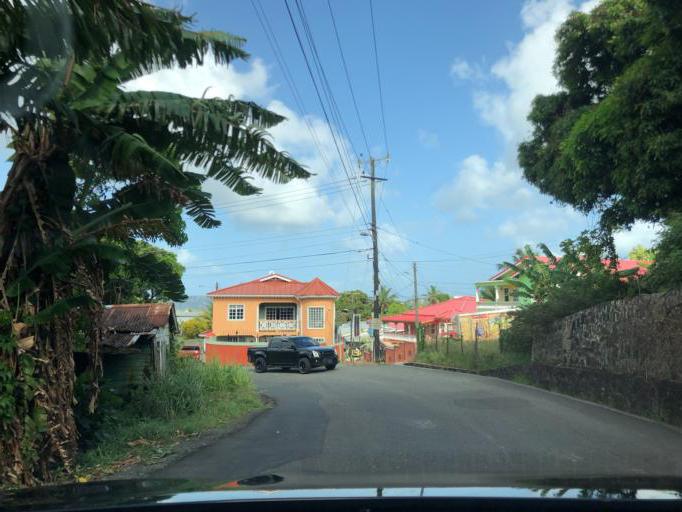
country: LC
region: Castries Quarter
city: Bisee
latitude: 14.0032
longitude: -60.9489
